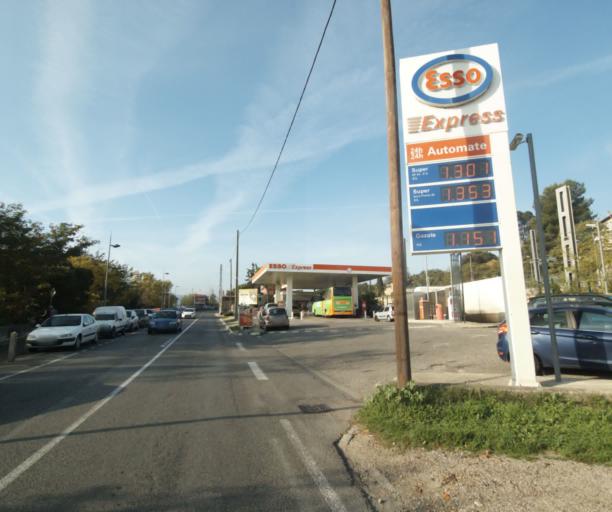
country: FR
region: Provence-Alpes-Cote d'Azur
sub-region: Departement des Bouches-du-Rhone
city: Aubagne
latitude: 43.2948
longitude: 5.5605
